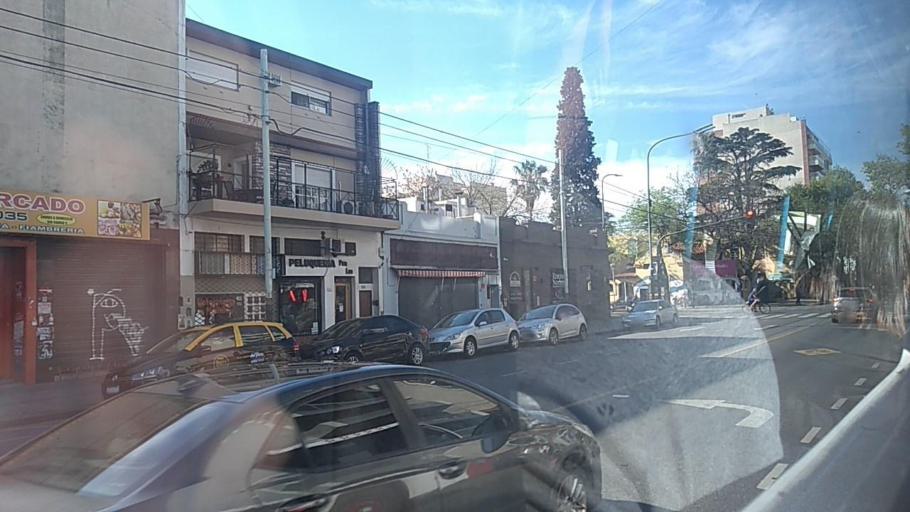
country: AR
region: Buenos Aires F.D.
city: Villa Santa Rita
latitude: -34.6039
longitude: -58.5088
